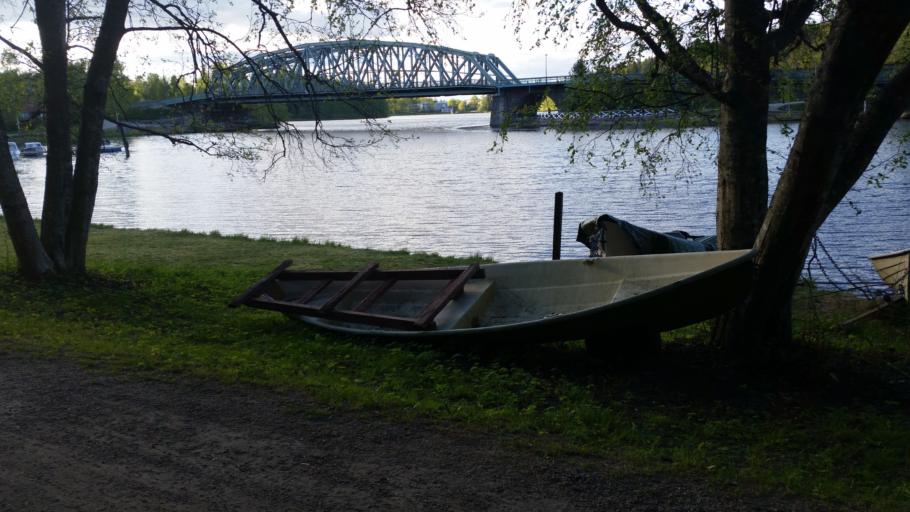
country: FI
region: Haeme
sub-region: Haemeenlinna
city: Haemeenlinna
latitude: 61.0134
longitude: 24.4481
